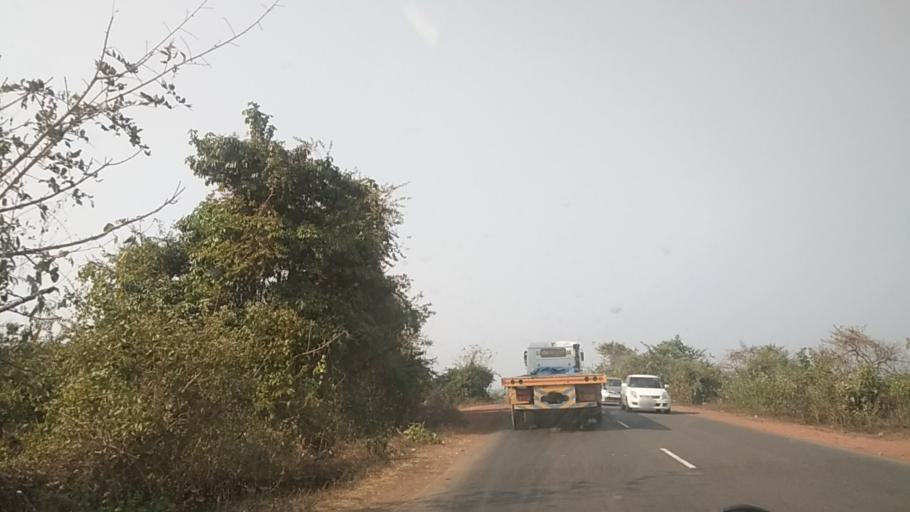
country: IN
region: Goa
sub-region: North Goa
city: Colovale
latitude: 15.6790
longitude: 73.8363
